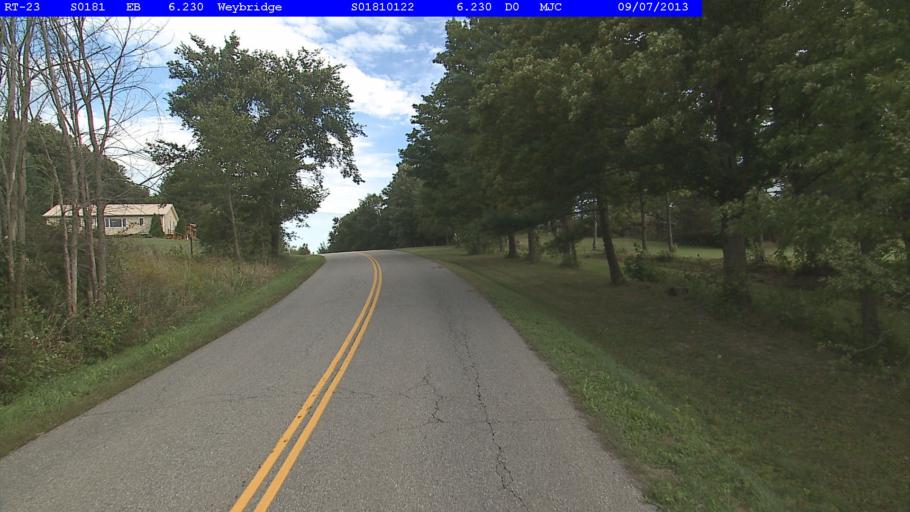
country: US
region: Vermont
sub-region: Addison County
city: Vergennes
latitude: 44.0792
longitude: -73.2509
